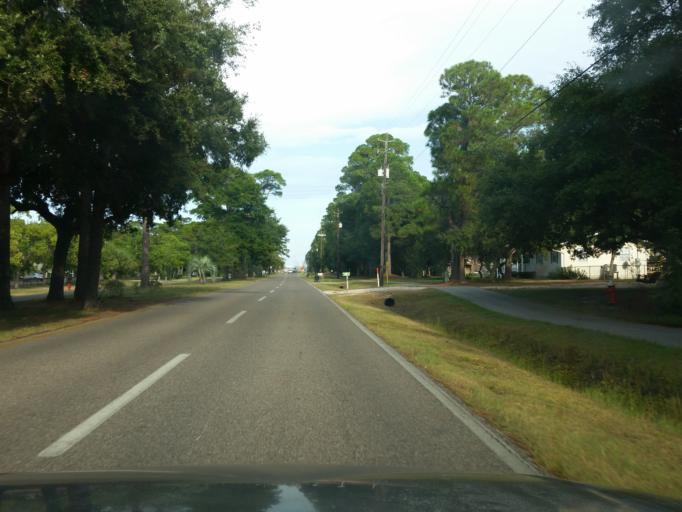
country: US
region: Alabama
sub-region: Mobile County
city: Dauphin Island
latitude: 30.2513
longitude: -88.0893
